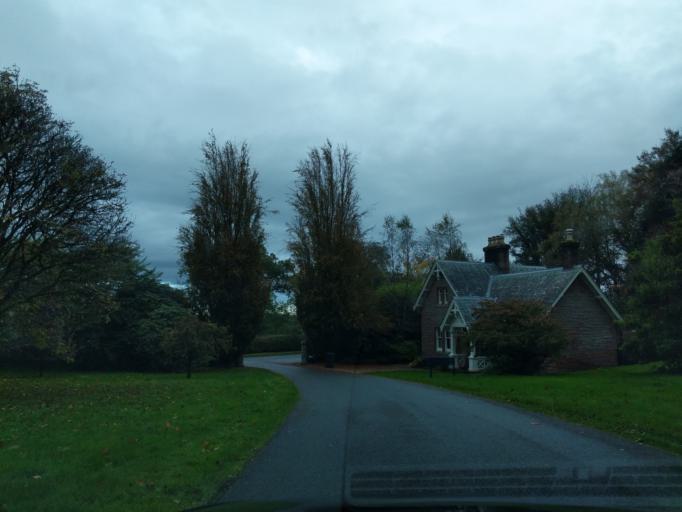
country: GB
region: Scotland
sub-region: Dumfries and Galloway
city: Castle Douglas
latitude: 54.9268
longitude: -3.9408
